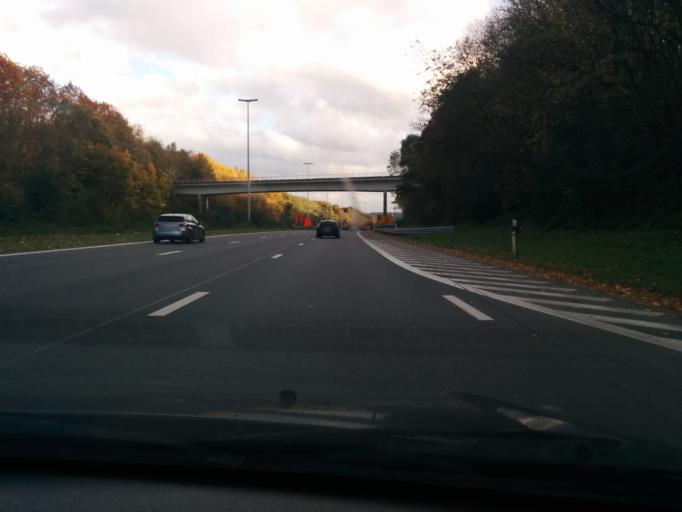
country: BE
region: Wallonia
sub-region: Province du Brabant Wallon
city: Braine-le-Chateau
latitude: 50.6954
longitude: 4.2904
